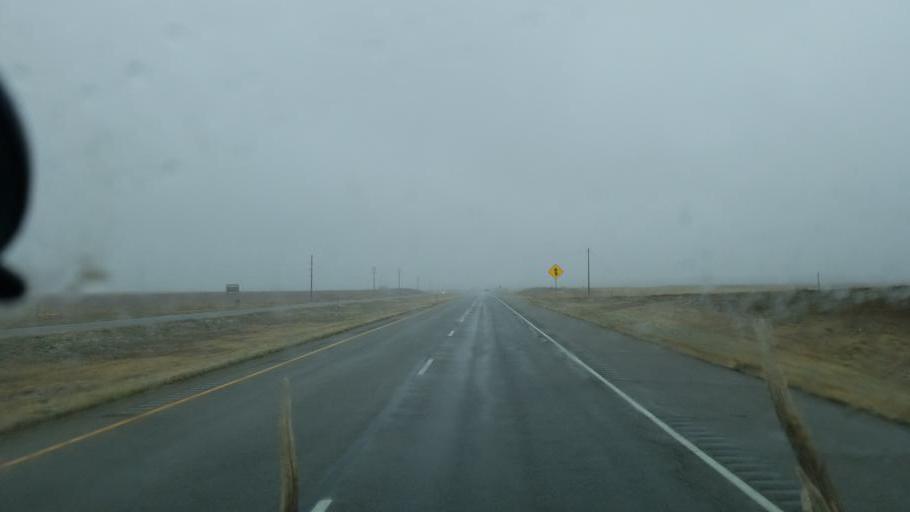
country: US
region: Colorado
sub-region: Pueblo County
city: Colorado City
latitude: 37.8616
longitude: -104.8286
